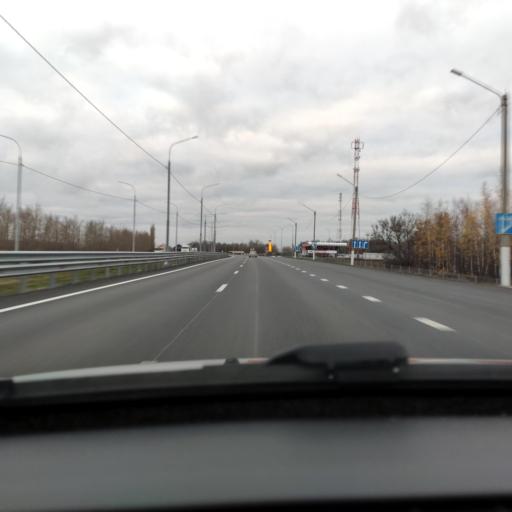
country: RU
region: Voronezj
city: Ramon'
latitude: 51.9901
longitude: 39.2174
